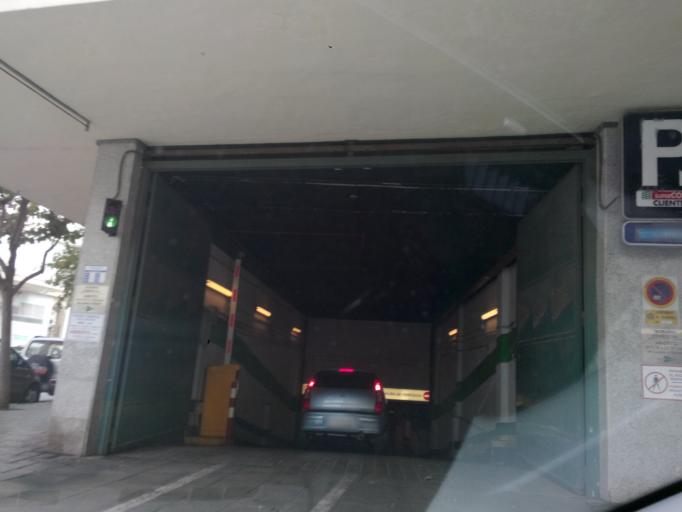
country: ES
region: Andalusia
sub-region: Provincia de Malaga
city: Fuengirola
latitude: 36.5543
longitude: -4.6155
